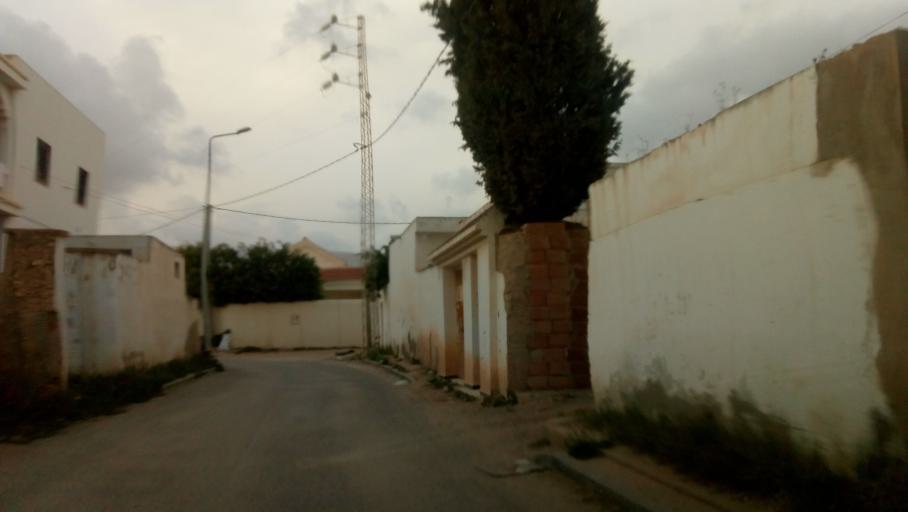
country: TN
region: Safaqis
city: Sfax
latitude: 34.7690
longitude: 10.7015
